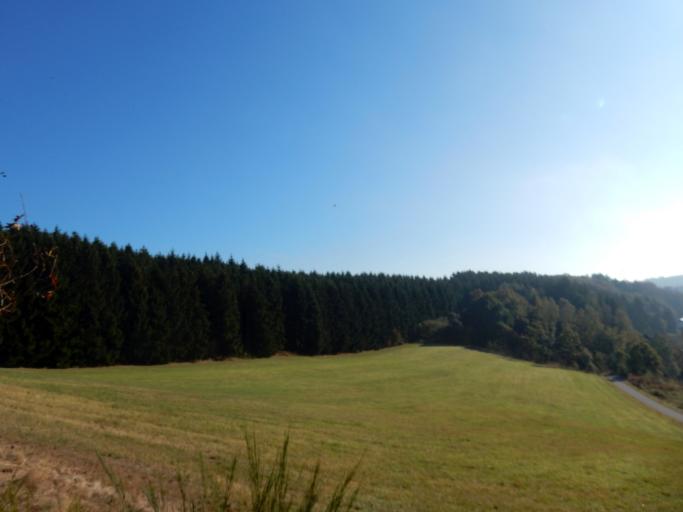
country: LU
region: Diekirch
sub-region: Canton de Clervaux
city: Troisvierges
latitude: 50.1220
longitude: 5.9862
